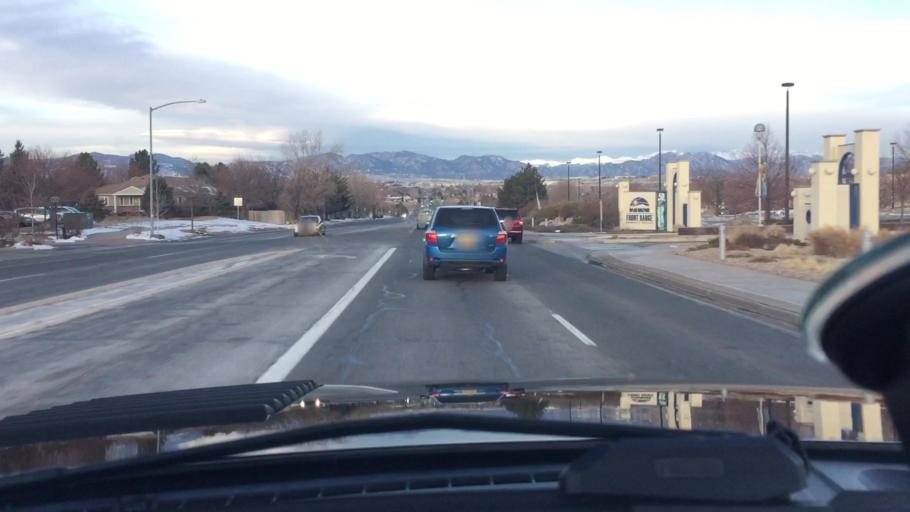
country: US
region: Colorado
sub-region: Adams County
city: Northglenn
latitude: 39.8997
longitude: -105.0377
